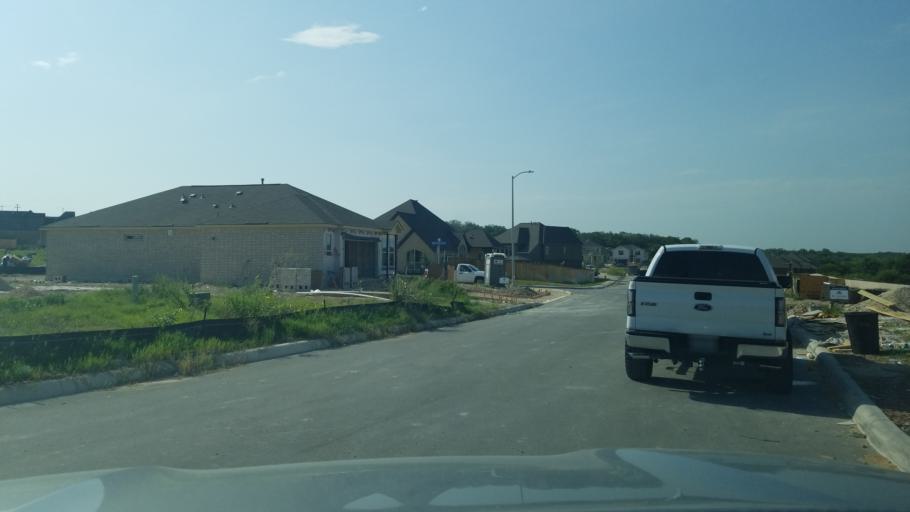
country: US
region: Texas
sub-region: Medina County
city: La Coste
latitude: 29.4084
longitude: -98.7881
